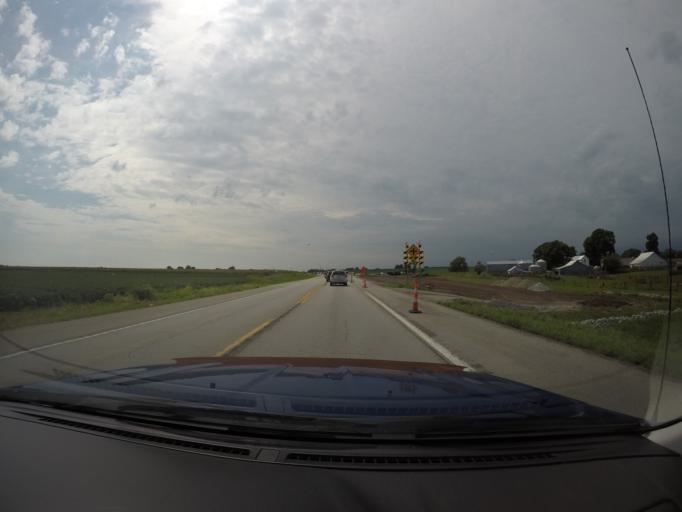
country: US
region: Missouri
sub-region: Lafayette County
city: Lexington
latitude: 39.1232
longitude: -93.9795
